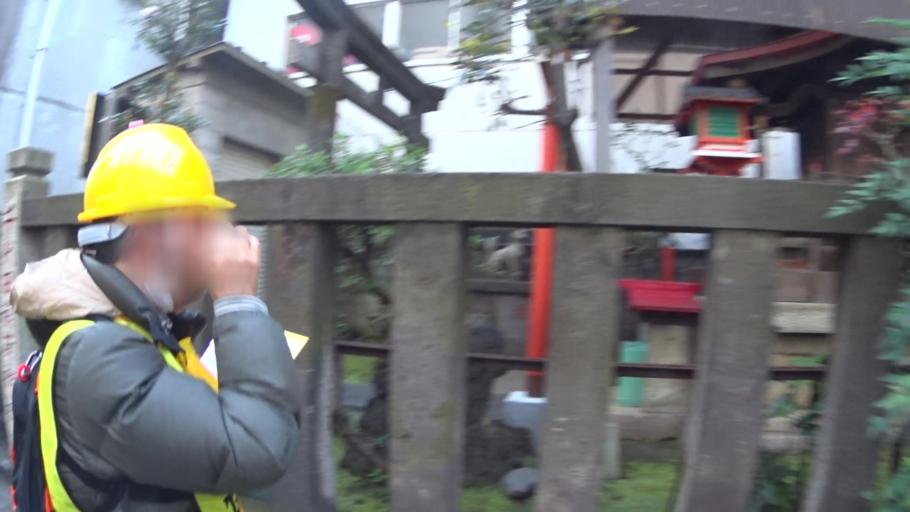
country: JP
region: Tokyo
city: Tokyo
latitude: 35.7011
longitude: 139.7776
